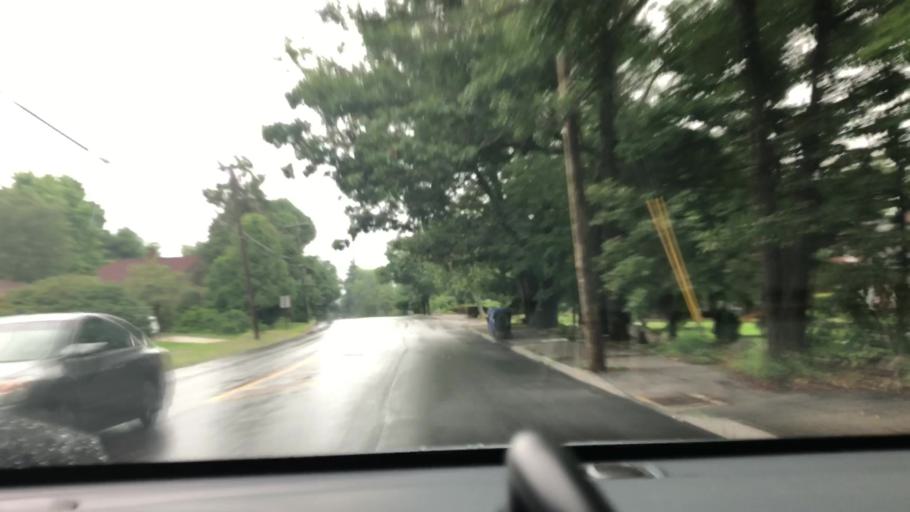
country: US
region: New Hampshire
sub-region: Hillsborough County
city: Manchester
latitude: 43.0184
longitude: -71.4622
